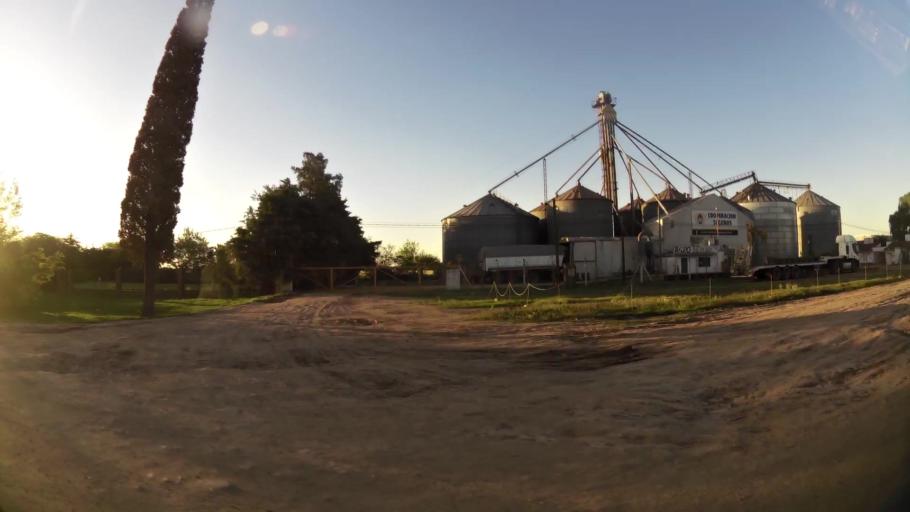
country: AR
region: Cordoba
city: La Playosa
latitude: -32.1030
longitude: -63.0361
